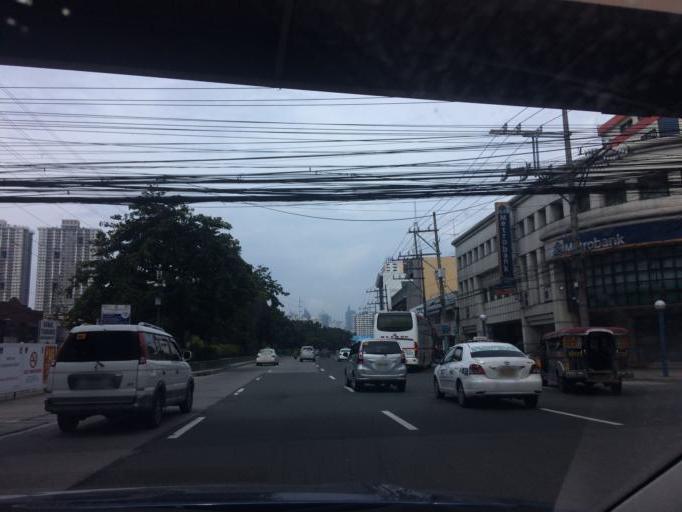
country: PH
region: Metro Manila
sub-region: City of Manila
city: Port Area
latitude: 14.5529
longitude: 120.9917
